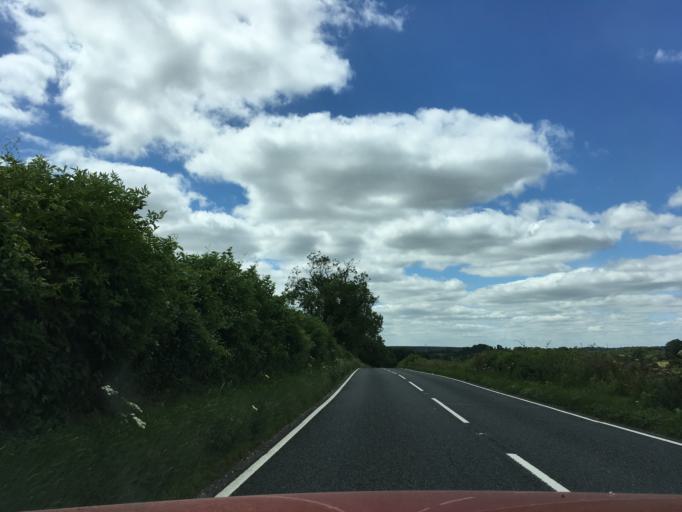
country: GB
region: England
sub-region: Hampshire
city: Highclere
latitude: 51.3011
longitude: -1.4040
